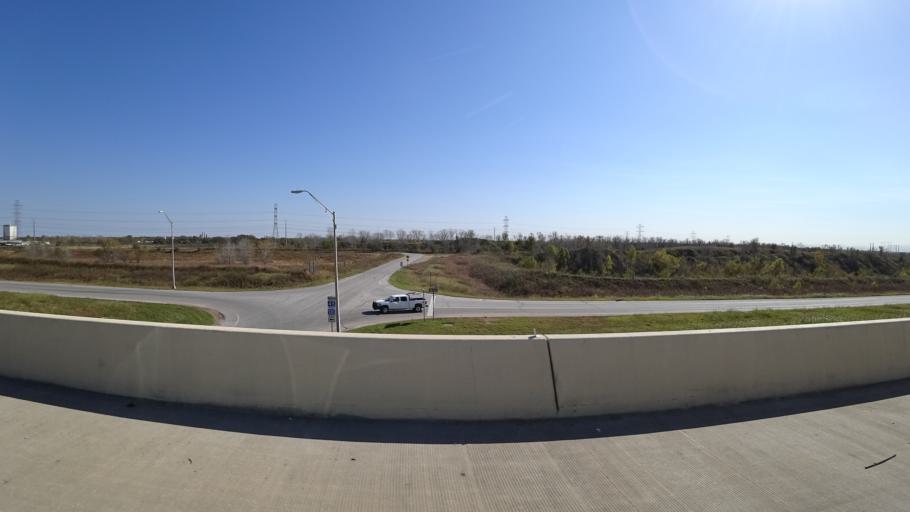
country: US
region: Texas
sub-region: Travis County
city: Hornsby Bend
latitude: 30.2285
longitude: -97.6199
